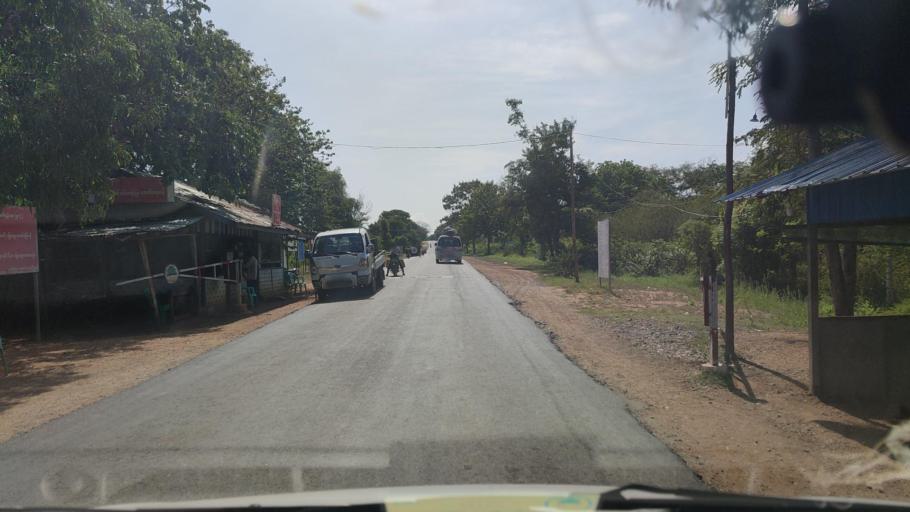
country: MM
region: Magway
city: Minbu
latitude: 20.1802
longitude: 94.8381
